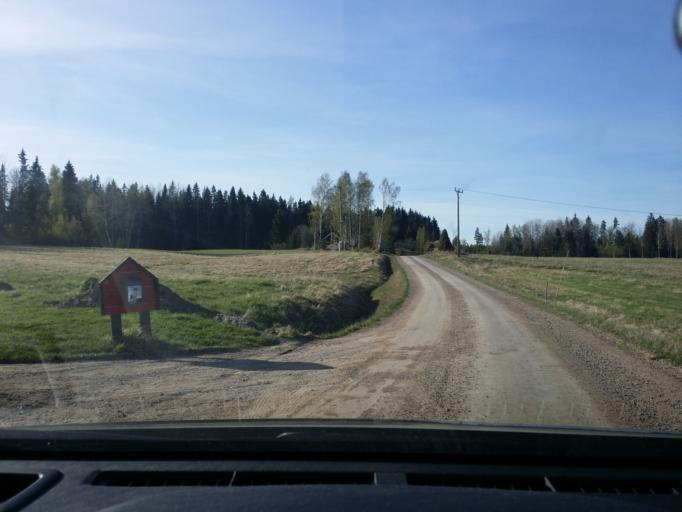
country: SE
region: Dalarna
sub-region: Avesta Kommun
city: Avesta
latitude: 60.0810
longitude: 16.3702
